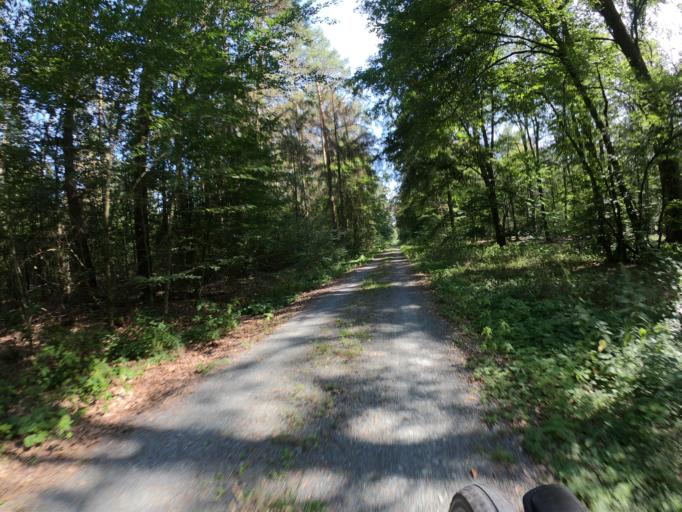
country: DE
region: Hesse
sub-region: Regierungsbezirk Darmstadt
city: Erzhausen
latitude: 49.9874
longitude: 8.6240
